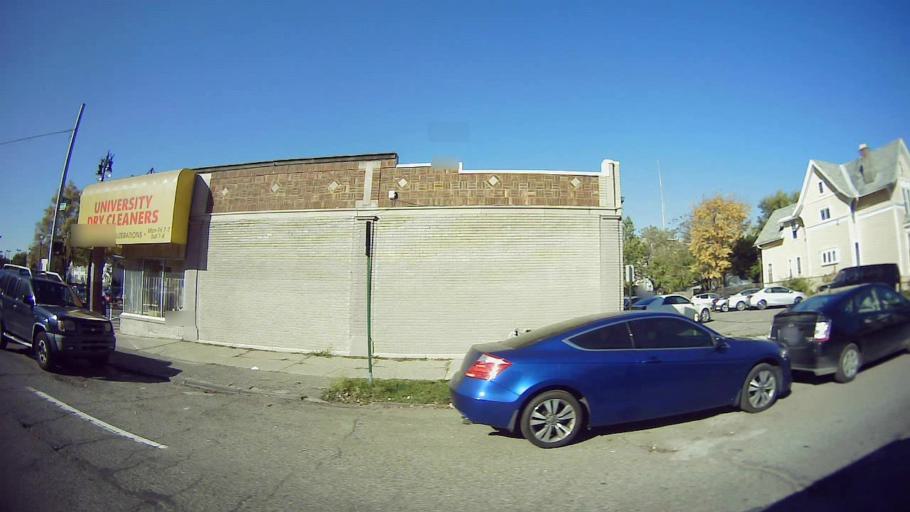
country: US
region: Michigan
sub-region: Wayne County
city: Detroit
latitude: 42.3538
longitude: -83.0651
